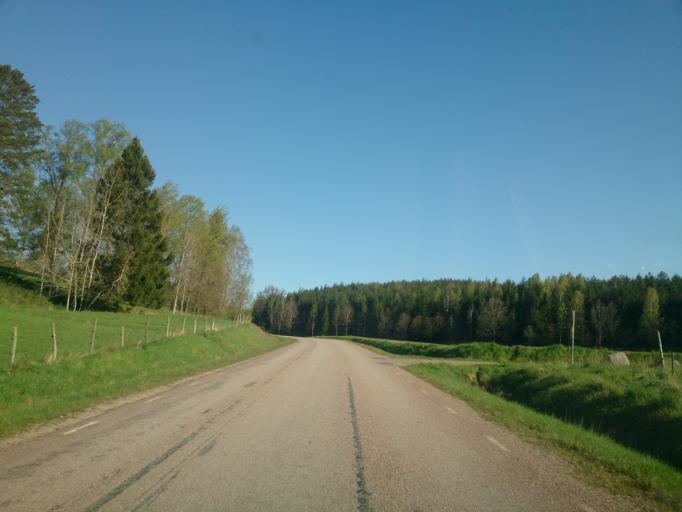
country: SE
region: OEstergoetland
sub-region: Linkopings Kommun
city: Ljungsbro
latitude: 58.5568
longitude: 15.5202
